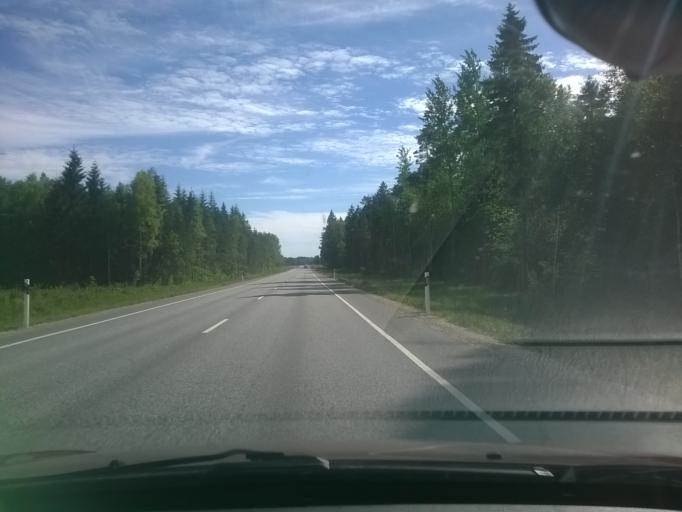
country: EE
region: Jaervamaa
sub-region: Paide linn
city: Paide
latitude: 58.9497
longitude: 25.6480
